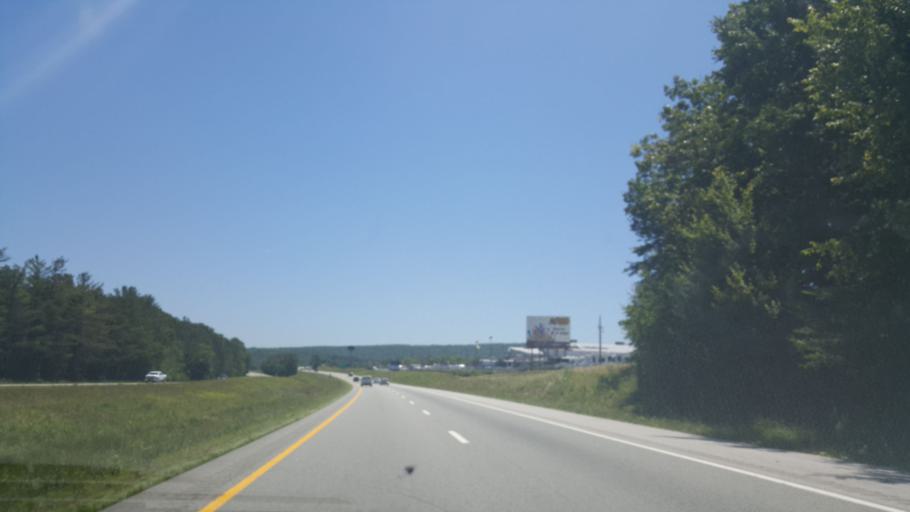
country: US
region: Tennessee
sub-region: Roane County
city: Rockwood
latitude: 35.8920
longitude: -84.7447
